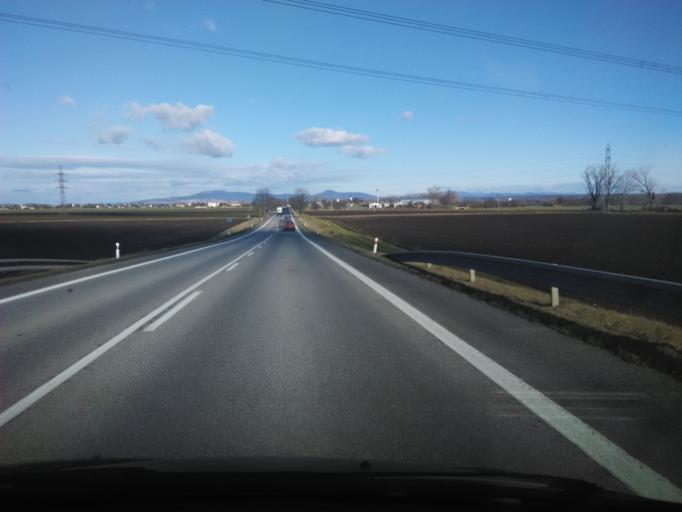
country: SK
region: Nitriansky
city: Surany
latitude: 48.1949
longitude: 18.1479
